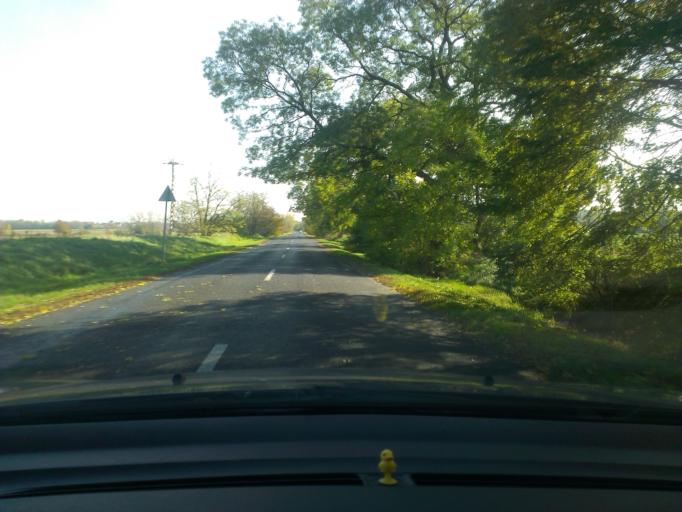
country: HU
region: Komarom-Esztergom
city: Mocsa
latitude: 47.7160
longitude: 18.1842
